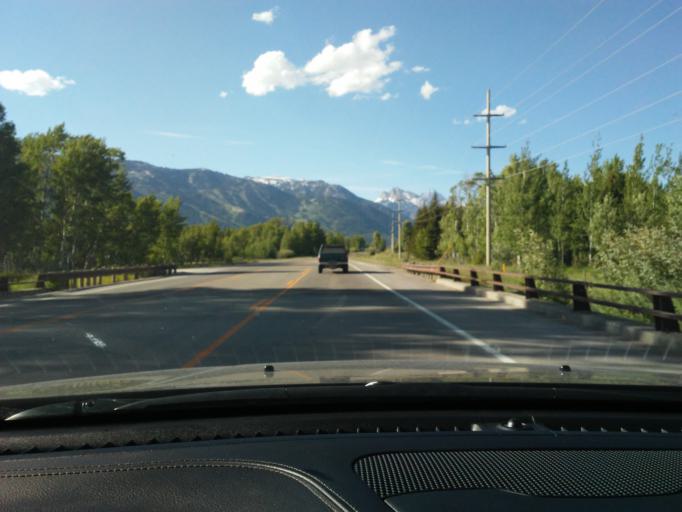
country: US
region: Wyoming
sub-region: Teton County
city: Moose Wilson Road
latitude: 43.5467
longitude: -110.8220
